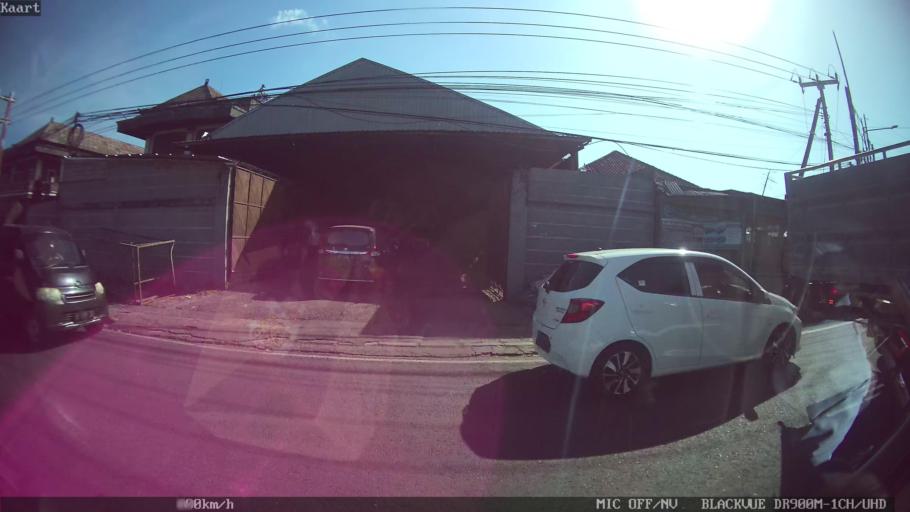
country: ID
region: Bali
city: Banjar Kertasari
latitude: -8.6190
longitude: 115.1907
